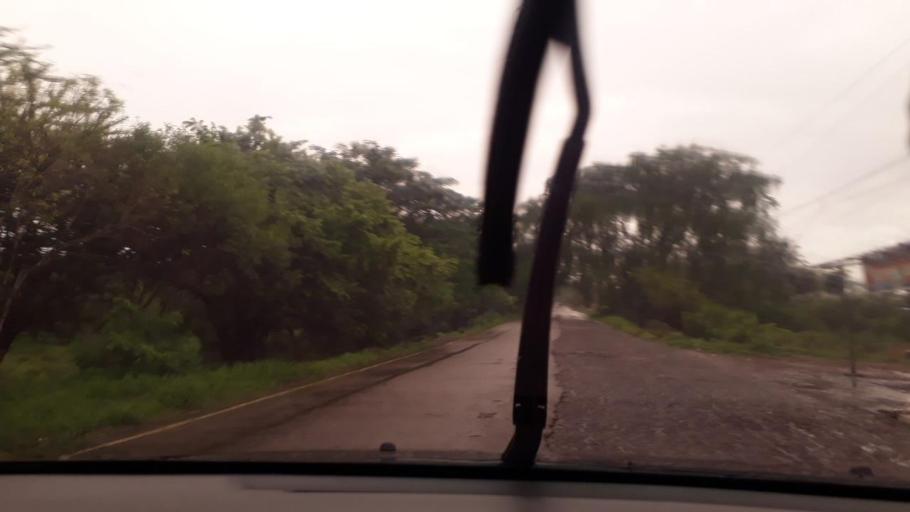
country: GT
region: Jutiapa
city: Comapa
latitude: 14.0557
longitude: -89.9382
